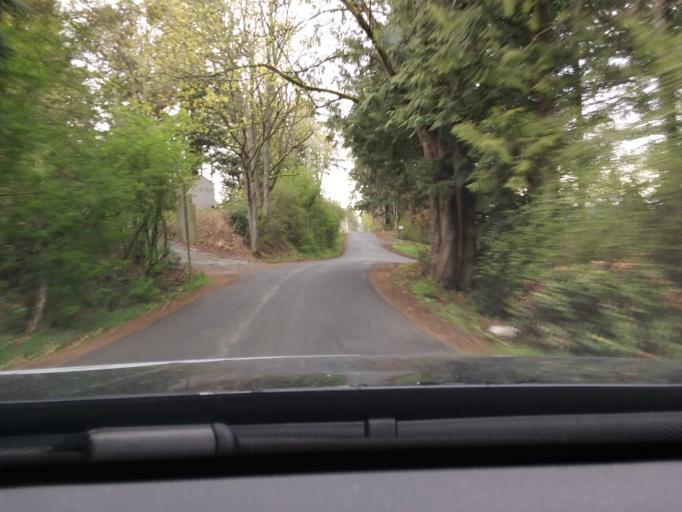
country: CA
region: British Columbia
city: Victoria
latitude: 48.5502
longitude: -123.3900
